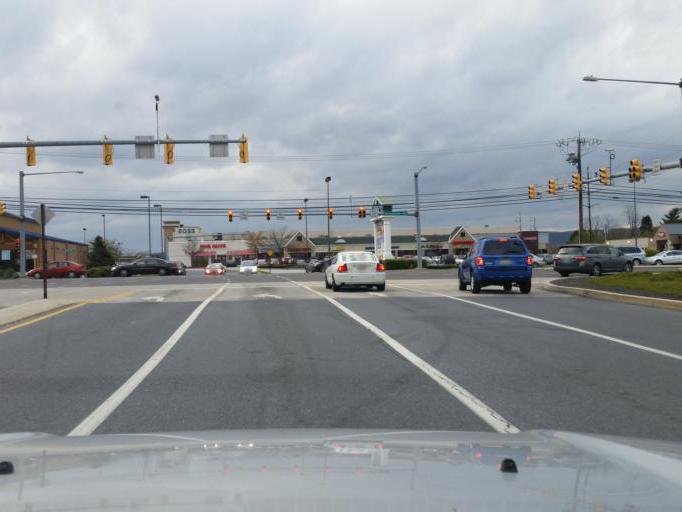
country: US
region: Pennsylvania
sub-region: Dauphin County
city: Paxtonia
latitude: 40.3112
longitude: -76.8008
